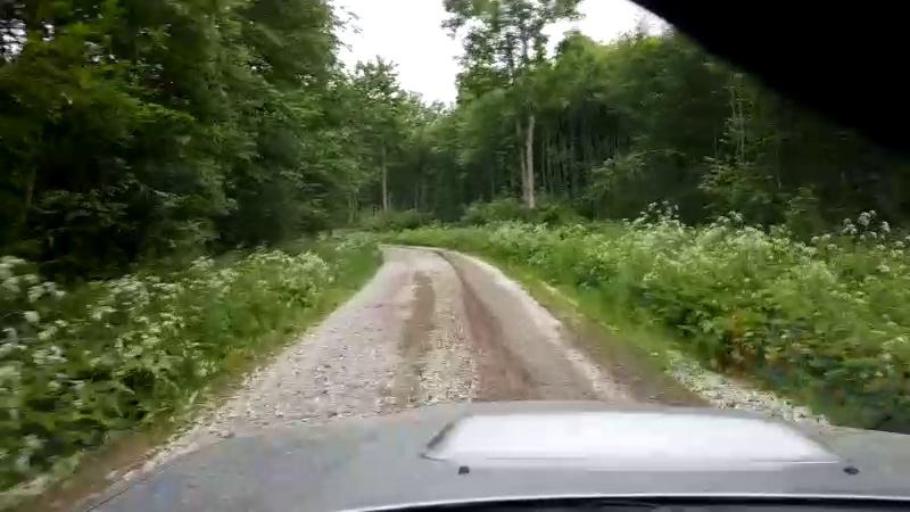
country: EE
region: Paernumaa
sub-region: Tootsi vald
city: Tootsi
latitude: 58.5939
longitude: 24.6632
